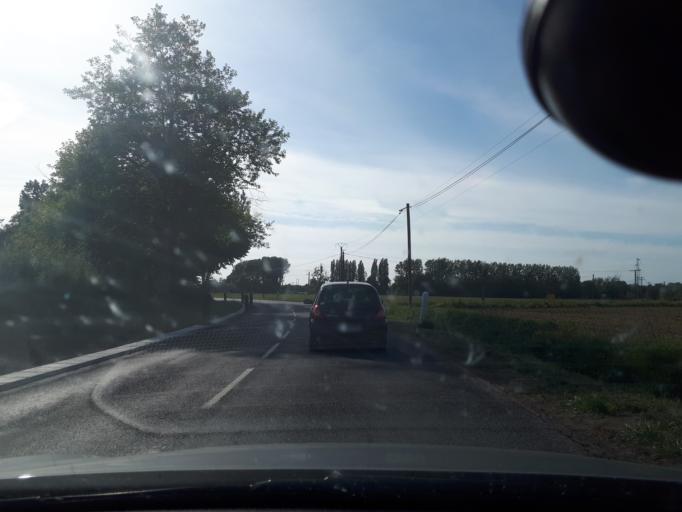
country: FR
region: Pays de la Loire
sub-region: Departement de la Sarthe
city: Champagne
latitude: 48.0776
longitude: 0.3312
